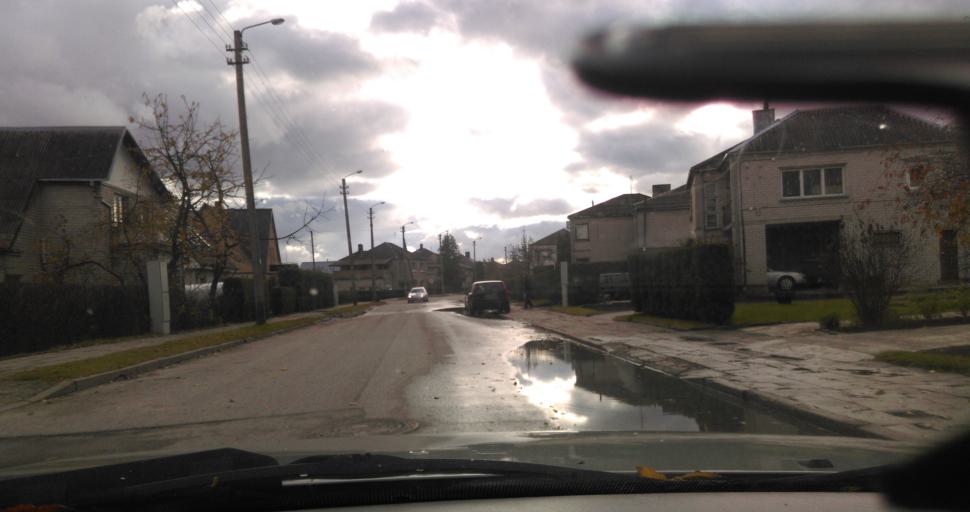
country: LT
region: Utenos apskritis
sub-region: Utena
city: Utena
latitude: 55.4922
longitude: 25.6014
